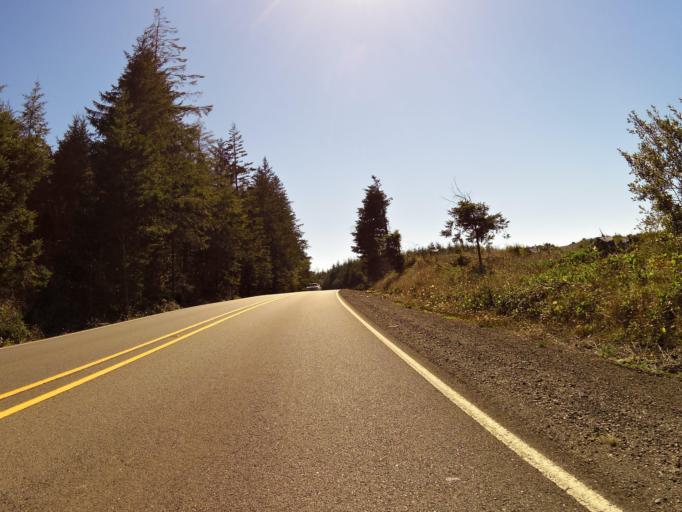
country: US
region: Oregon
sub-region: Coos County
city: Barview
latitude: 43.2536
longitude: -124.3368
